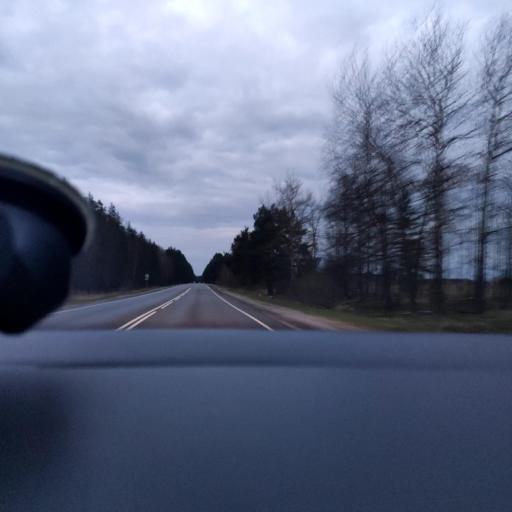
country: RU
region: Moskovskaya
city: Krasnyy Tkach
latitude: 55.4201
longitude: 39.1831
